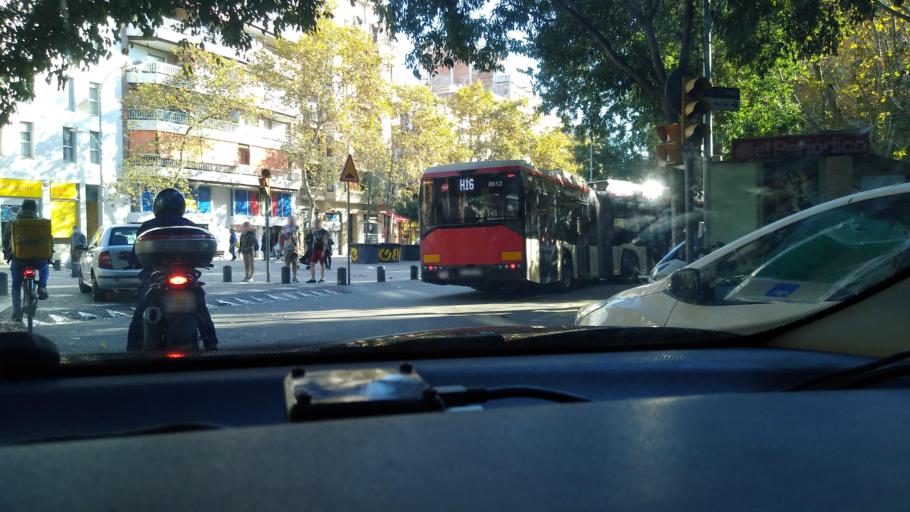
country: ES
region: Catalonia
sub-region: Provincia de Barcelona
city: Eixample
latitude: 41.3806
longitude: 2.1631
